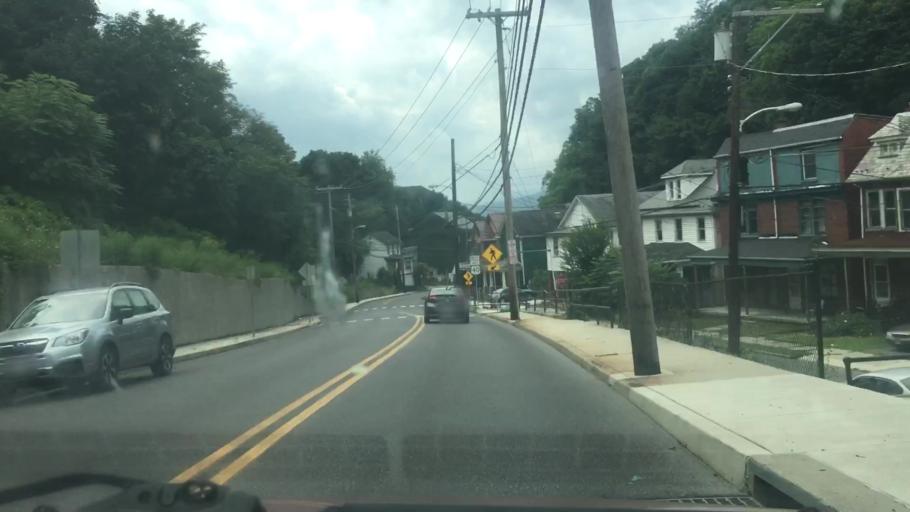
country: US
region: Maryland
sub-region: Allegany County
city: Cumberland
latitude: 39.6558
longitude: -78.7545
